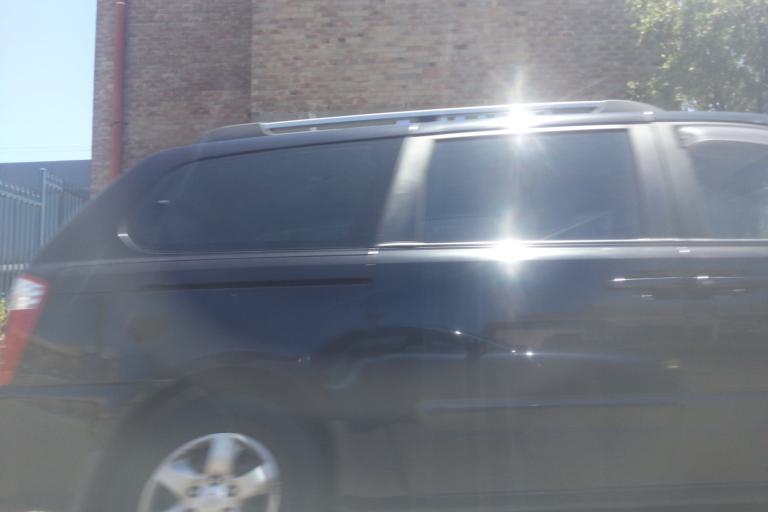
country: AU
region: New South Wales
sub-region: Wollongong
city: Wollongong
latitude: -34.4286
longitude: 150.8892
